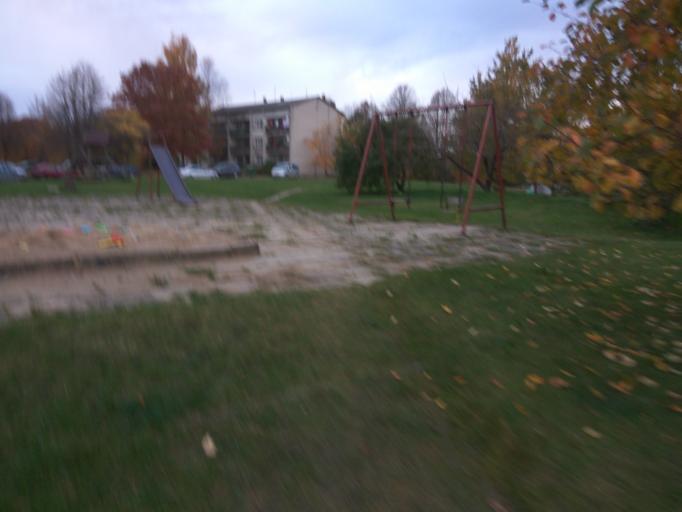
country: LV
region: Aizpute
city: Aizpute
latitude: 56.8353
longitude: 21.7745
